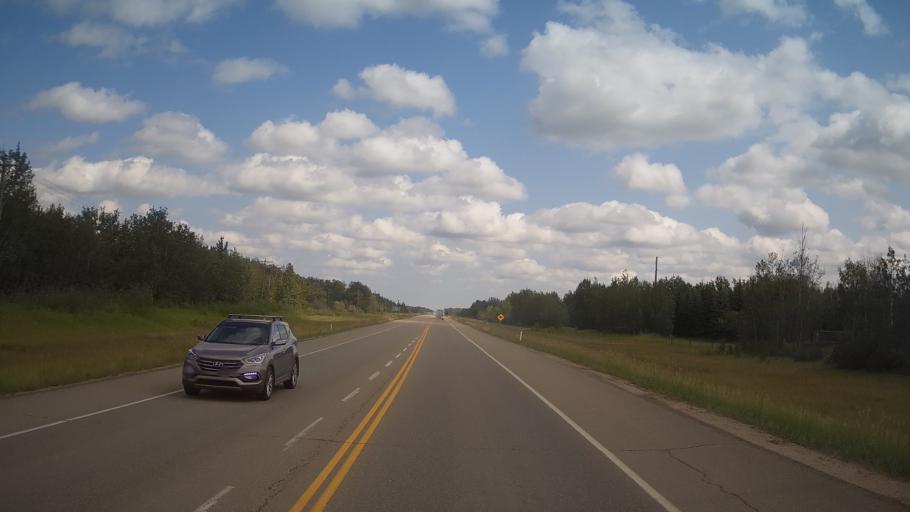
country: CA
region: Alberta
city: Sherwood Park
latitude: 53.3957
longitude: -113.0940
